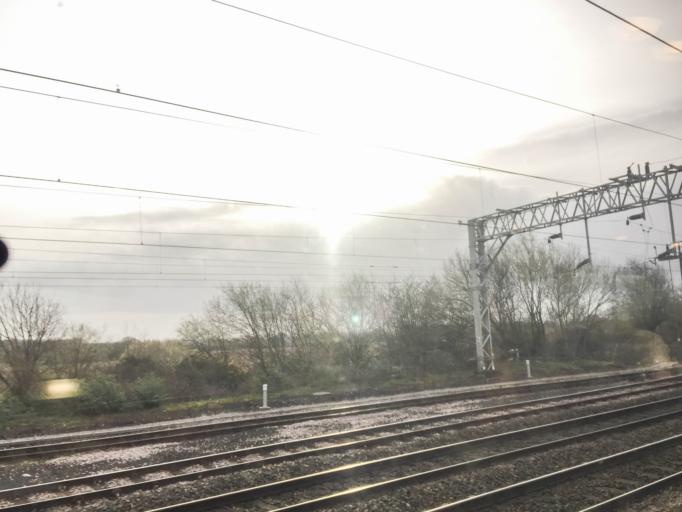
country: GB
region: England
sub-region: Cheshire East
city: Weston
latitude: 53.0762
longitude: -2.4251
